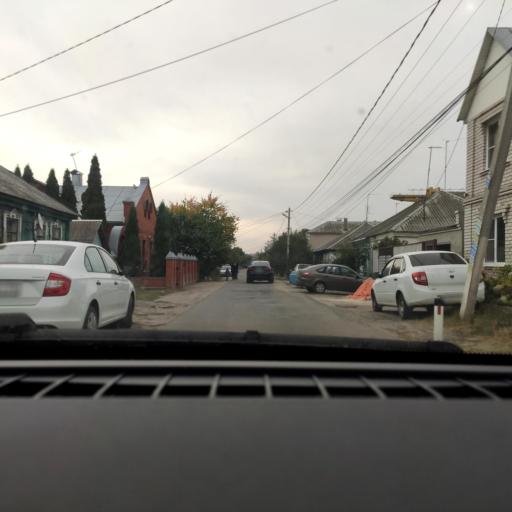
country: RU
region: Voronezj
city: Voronezh
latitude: 51.6737
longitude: 39.2600
